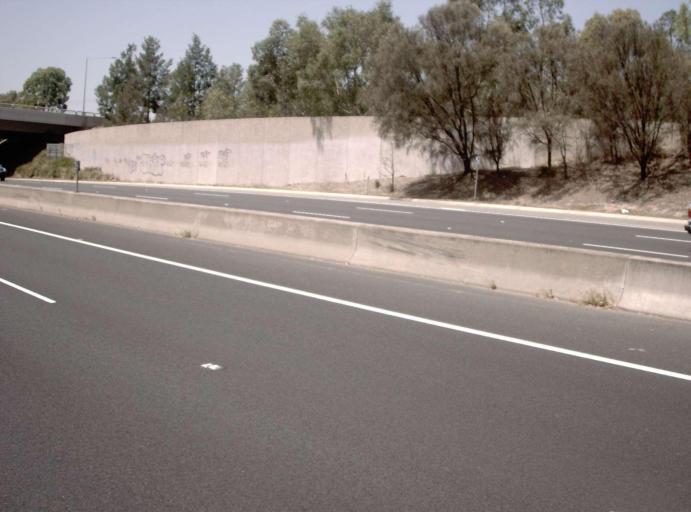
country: AU
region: Victoria
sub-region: Whitehorse
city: Box Hill North
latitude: -37.7972
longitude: 145.1257
